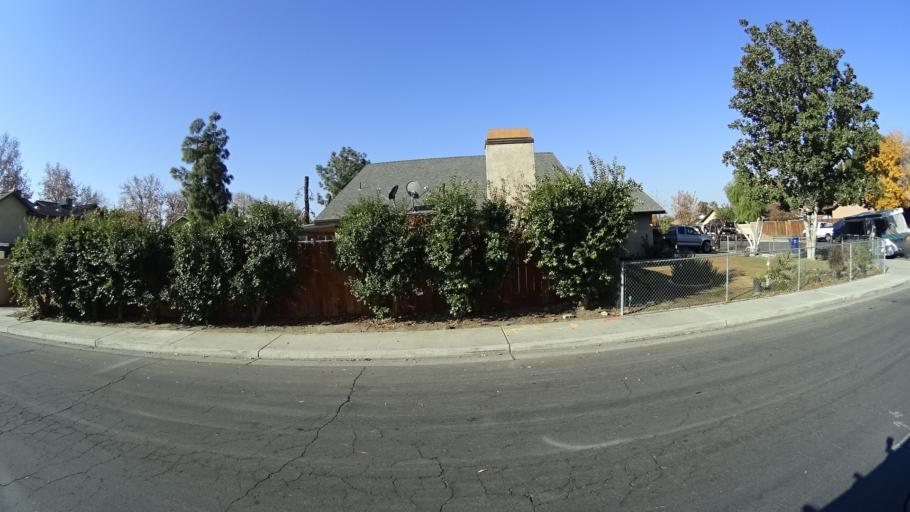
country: US
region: California
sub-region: Kern County
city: Greenfield
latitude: 35.3037
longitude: -119.0148
